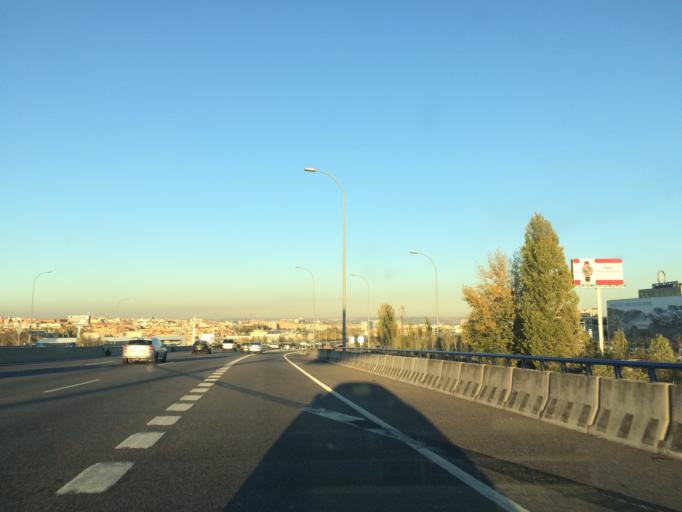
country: ES
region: Madrid
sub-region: Provincia de Madrid
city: Alcobendas
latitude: 40.5303
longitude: -3.6444
